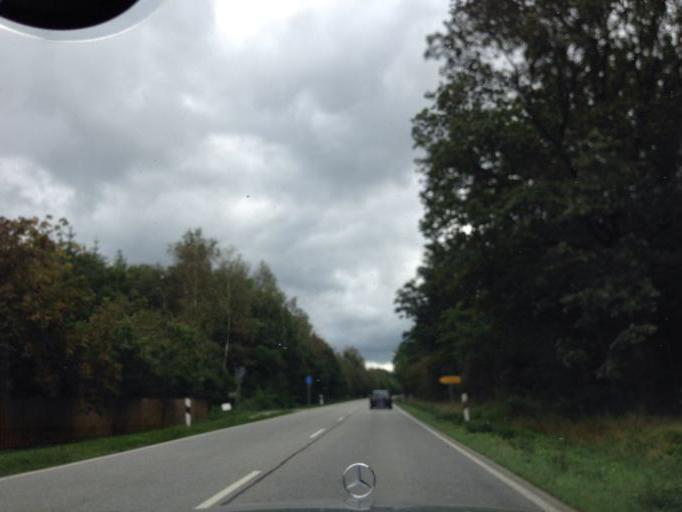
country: DE
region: Schleswig-Holstein
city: Leck
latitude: 54.7518
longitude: 9.0085
